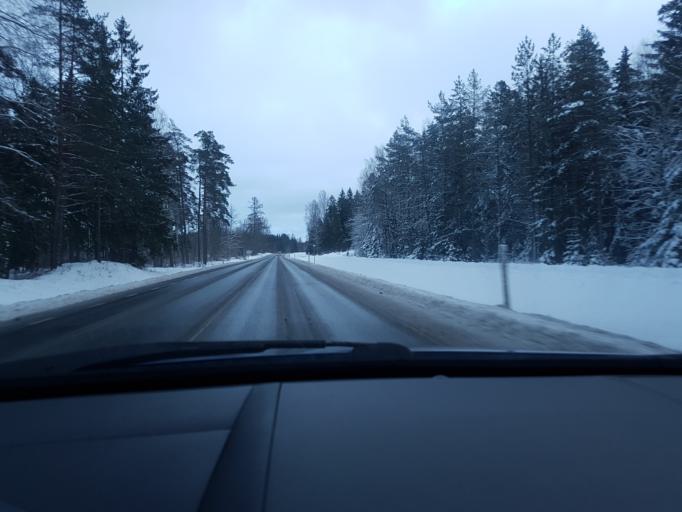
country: EE
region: Harju
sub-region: Kiili vald
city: Kiili
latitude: 59.3522
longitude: 24.7881
